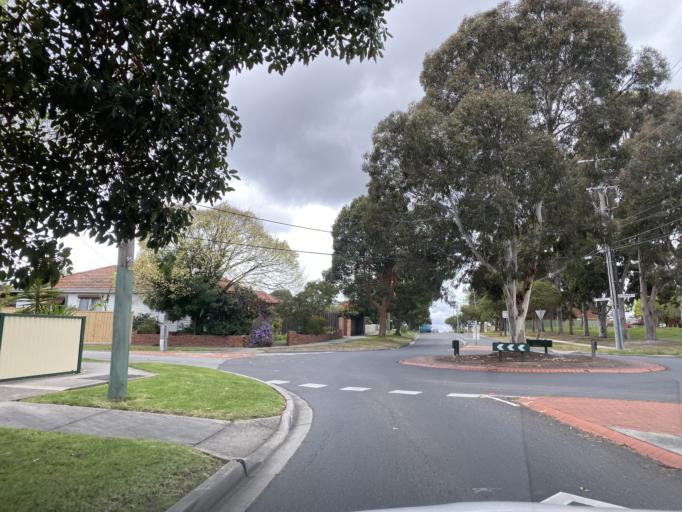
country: AU
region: Victoria
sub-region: Whitehorse
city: Burwood
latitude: -37.8455
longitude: 145.1310
